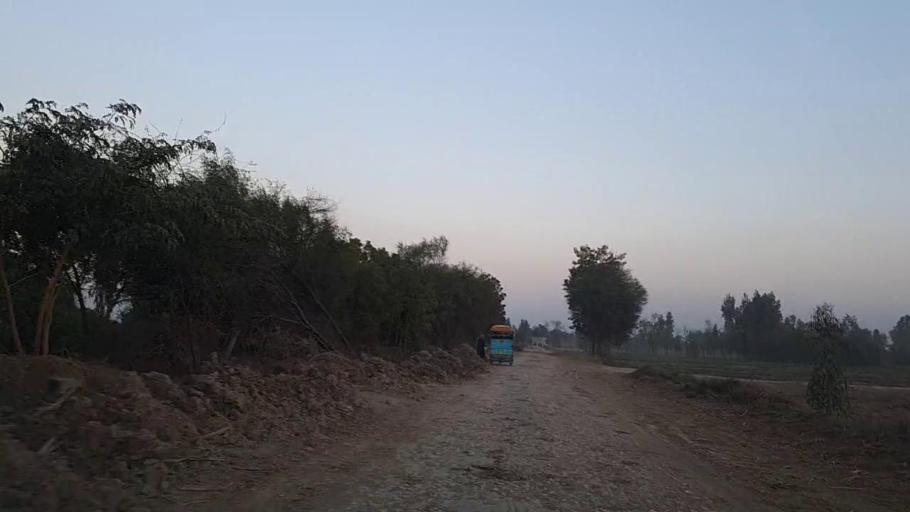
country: PK
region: Sindh
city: Naushahro Firoz
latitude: 26.7994
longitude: 68.0313
